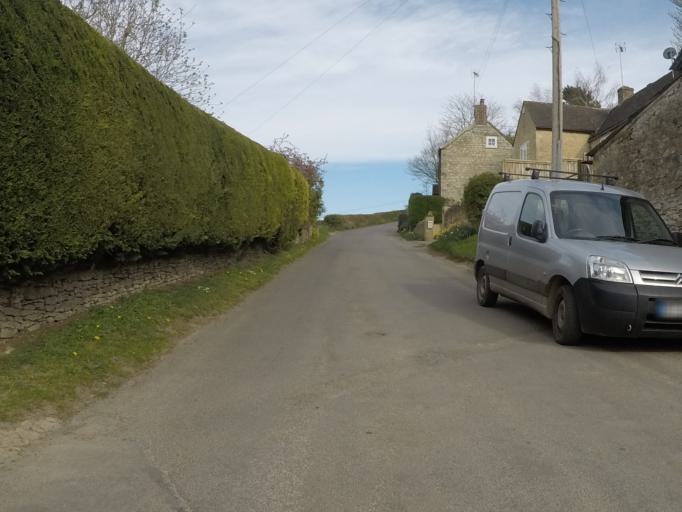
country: GB
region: England
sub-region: Oxfordshire
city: Charlbury
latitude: 51.8428
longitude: -1.4762
